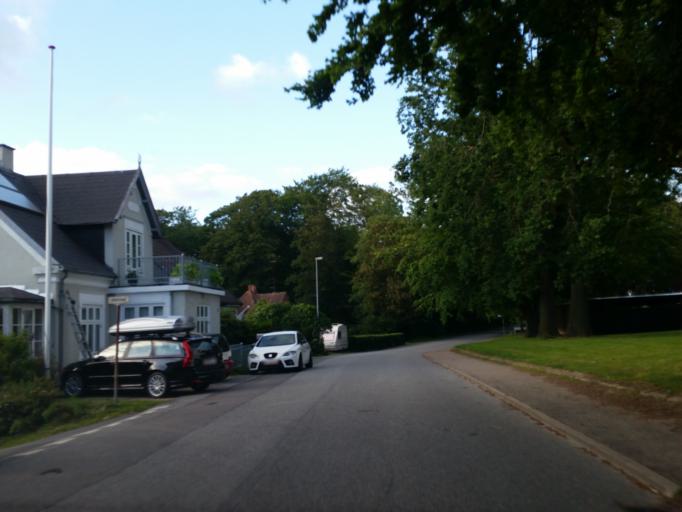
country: DK
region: South Denmark
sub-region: Vejle Kommune
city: Brejning
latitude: 55.6707
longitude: 9.6762
